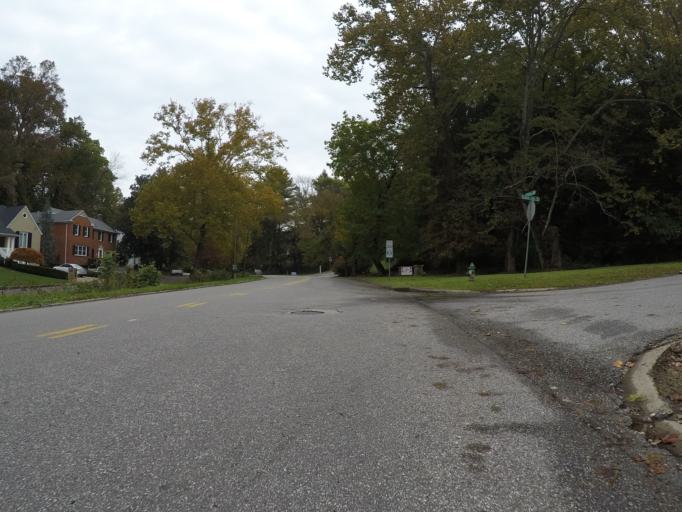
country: US
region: West Virginia
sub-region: Cabell County
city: Huntington
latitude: 38.4019
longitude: -82.4168
